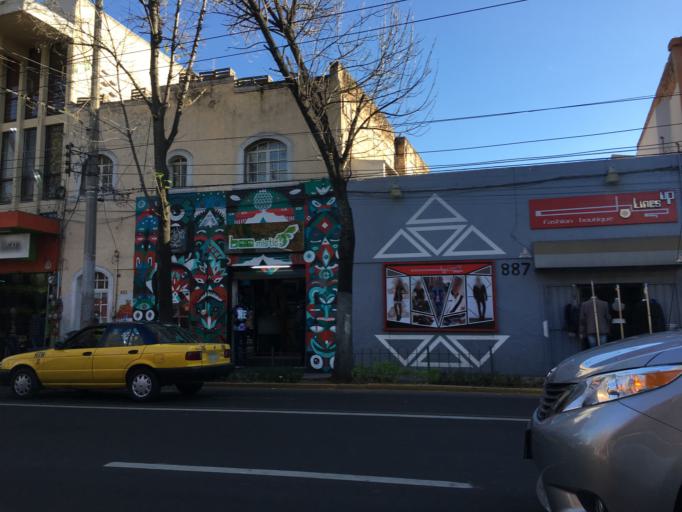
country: MX
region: Jalisco
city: Guadalajara
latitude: 20.6772
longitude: -103.3572
